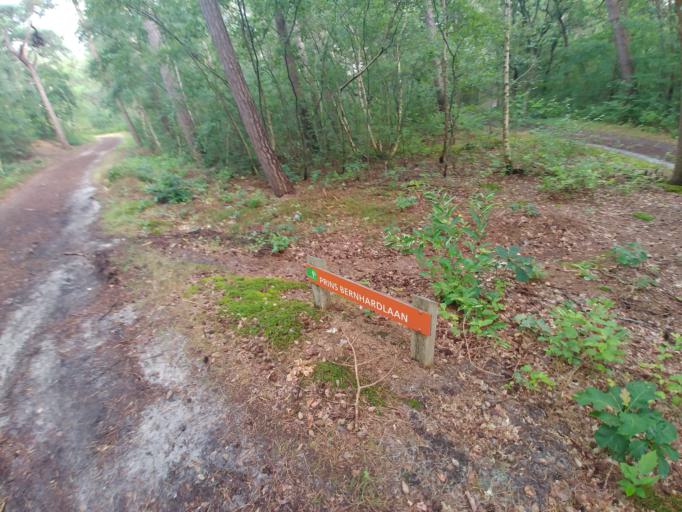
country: NL
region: North Holland
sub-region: Gemeente Bergen
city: Egmond aan Zee
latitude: 52.6889
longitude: 4.6795
